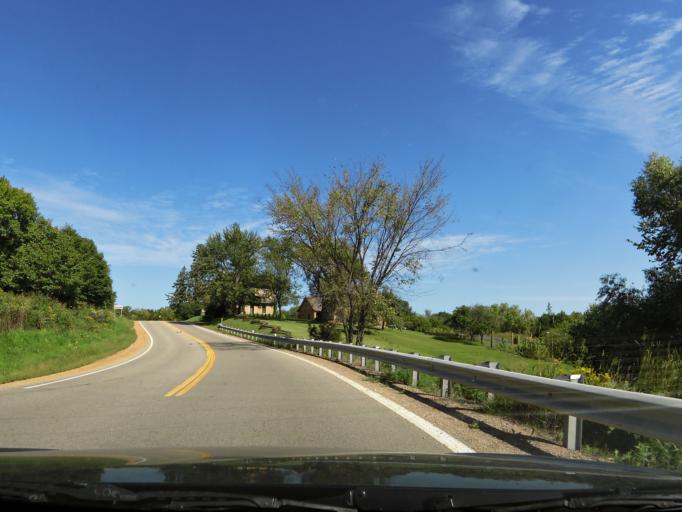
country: US
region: Minnesota
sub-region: Scott County
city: Shakopee
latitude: 44.8190
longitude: -93.5373
